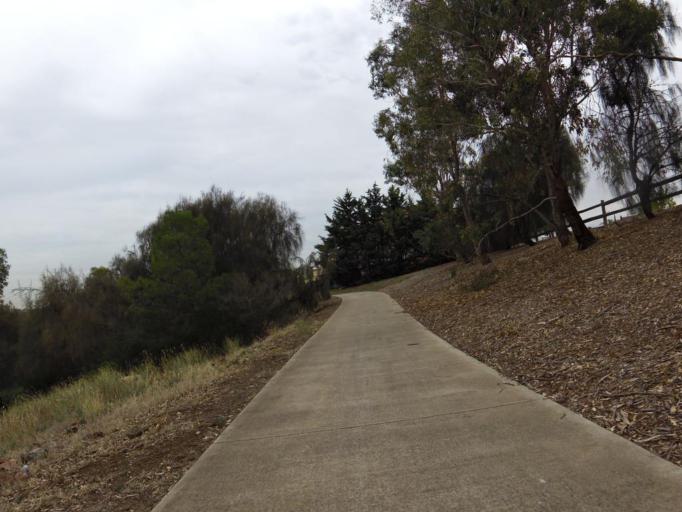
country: AU
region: Victoria
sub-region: Brimbank
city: Keilor Downs
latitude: -37.7129
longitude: 144.8171
